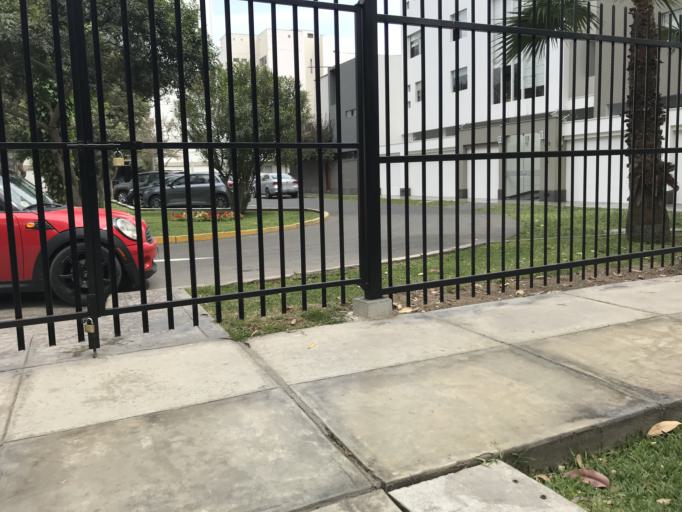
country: PE
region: Lima
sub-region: Lima
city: San Isidro
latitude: -12.1125
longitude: -77.0435
